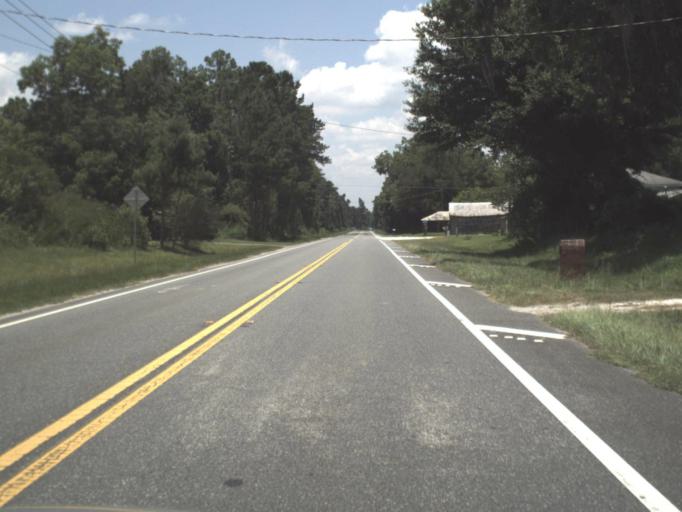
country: US
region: Florida
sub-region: Bradford County
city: Starke
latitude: 30.0217
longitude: -82.1526
